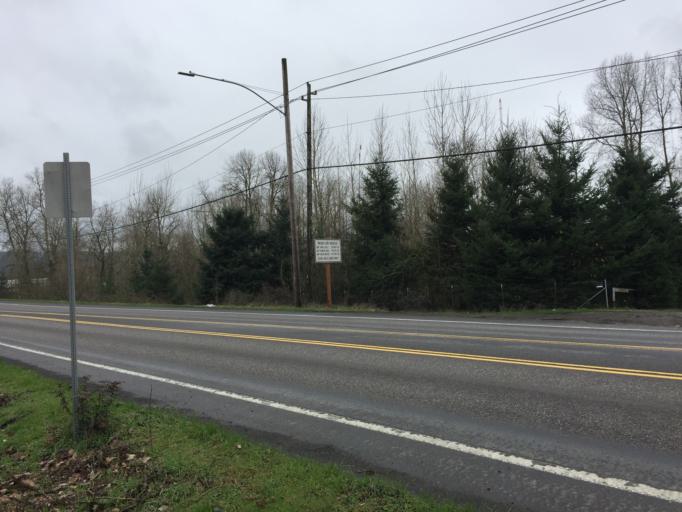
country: US
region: Washington
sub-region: Clark County
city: Vancouver
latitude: 45.6017
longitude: -122.7178
